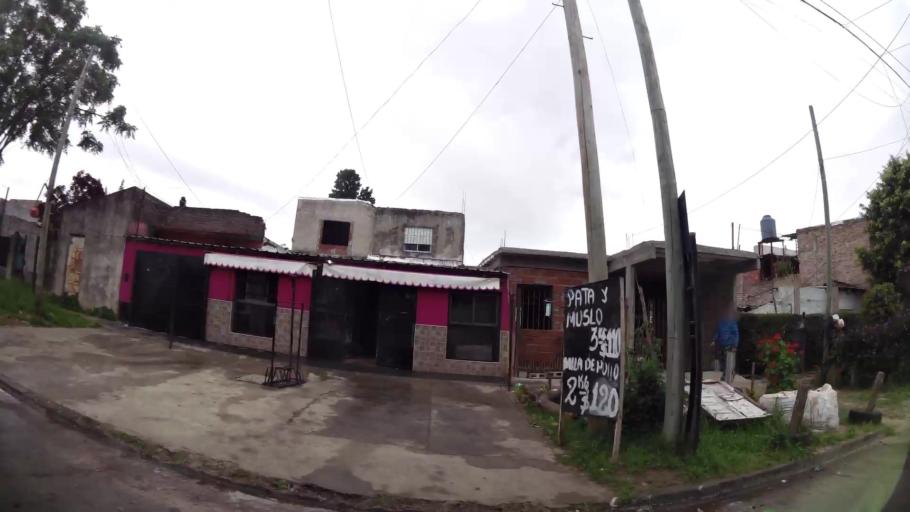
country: AR
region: Buenos Aires
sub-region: Partido de Quilmes
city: Quilmes
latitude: -34.7582
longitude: -58.2296
